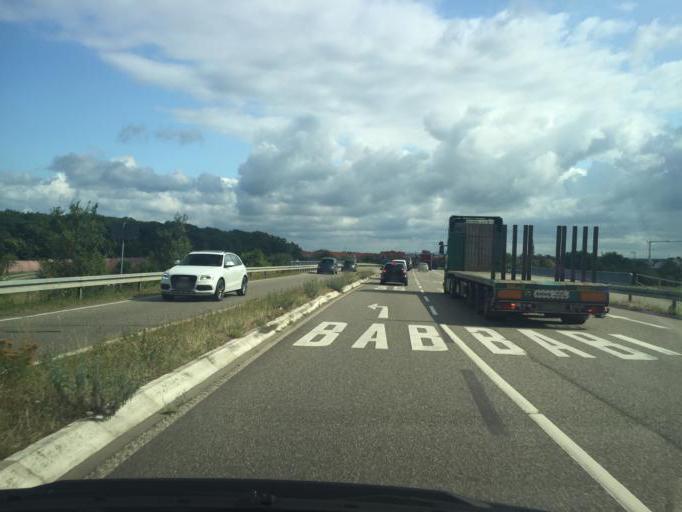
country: DE
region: Baden-Wuerttemberg
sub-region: Karlsruhe Region
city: Forst
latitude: 49.1421
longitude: 8.5774
